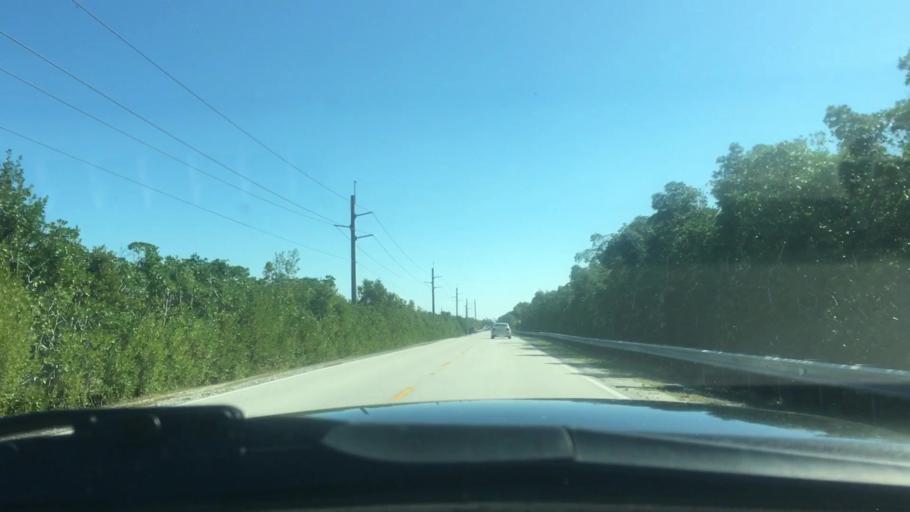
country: US
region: Florida
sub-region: Monroe County
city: North Key Largo
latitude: 25.2807
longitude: -80.3475
